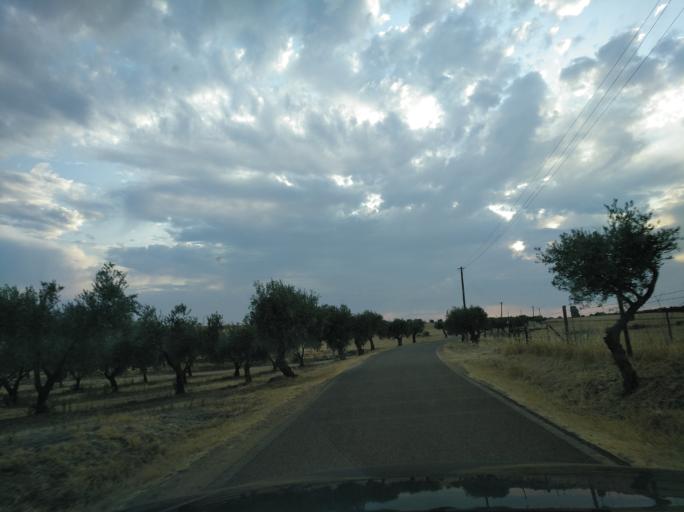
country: PT
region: Portalegre
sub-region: Campo Maior
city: Campo Maior
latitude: 39.0164
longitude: -7.0367
